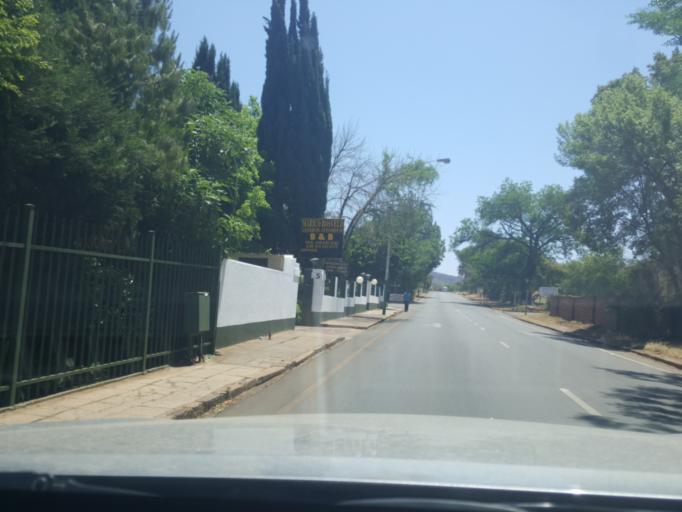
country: ZA
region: North-West
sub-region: Ngaka Modiri Molema District Municipality
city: Zeerust
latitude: -25.5420
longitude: 26.0781
